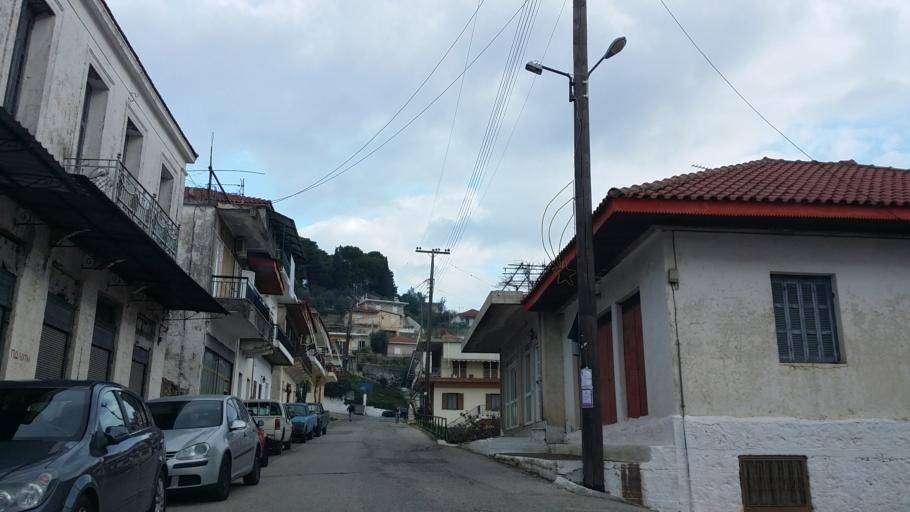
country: GR
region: West Greece
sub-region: Nomos Aitolias kai Akarnanias
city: Katouna
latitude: 38.7846
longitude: 21.1127
